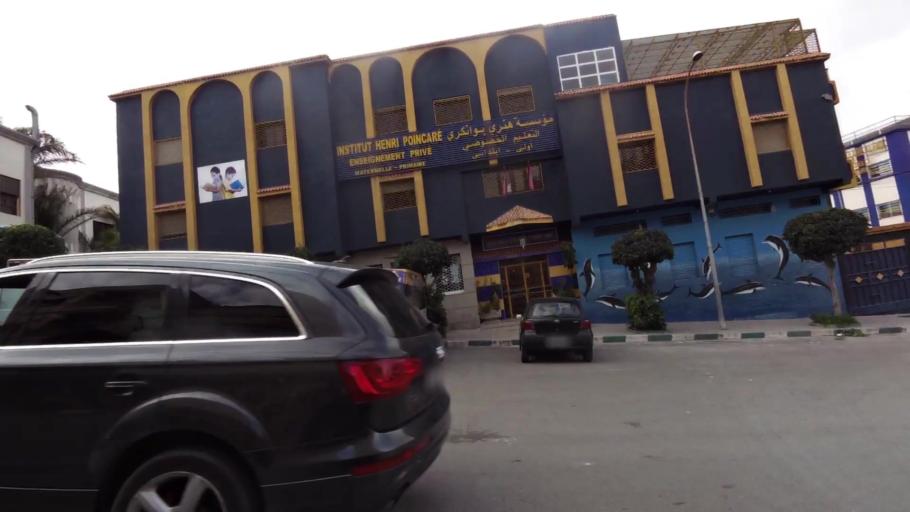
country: MA
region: Tanger-Tetouan
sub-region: Tanger-Assilah
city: Tangier
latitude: 35.7631
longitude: -5.7986
